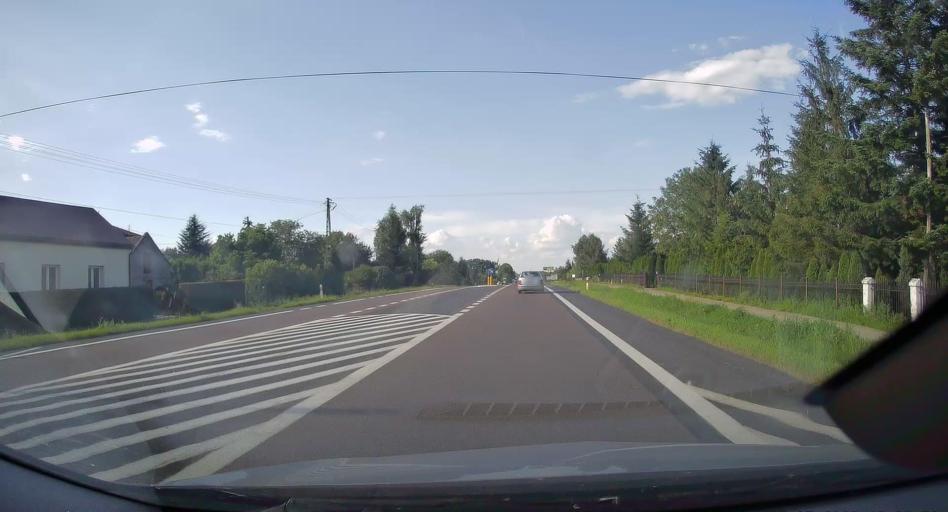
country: PL
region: Subcarpathian Voivodeship
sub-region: Powiat przemyski
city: Orly
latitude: 49.8635
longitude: 22.8085
